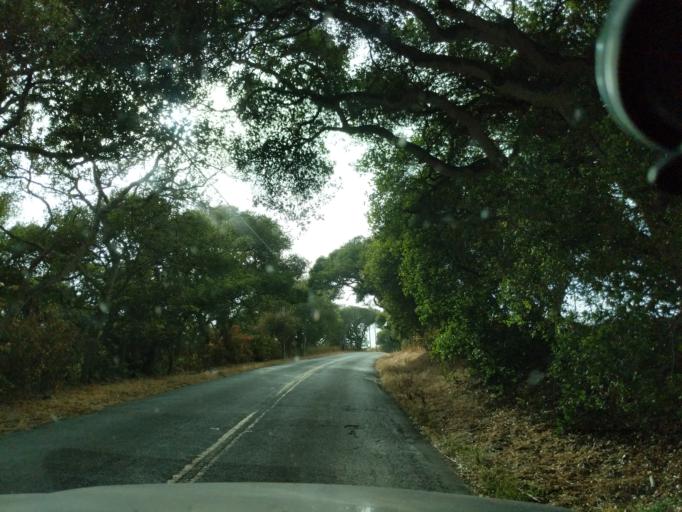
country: US
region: California
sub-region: Monterey County
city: Elkhorn
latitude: 36.8169
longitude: -121.7260
